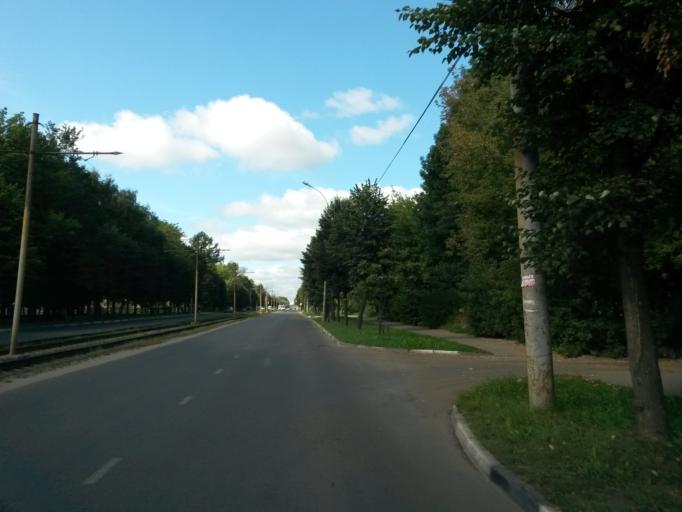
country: RU
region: Jaroslavl
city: Yaroslavl
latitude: 57.6375
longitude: 39.8559
